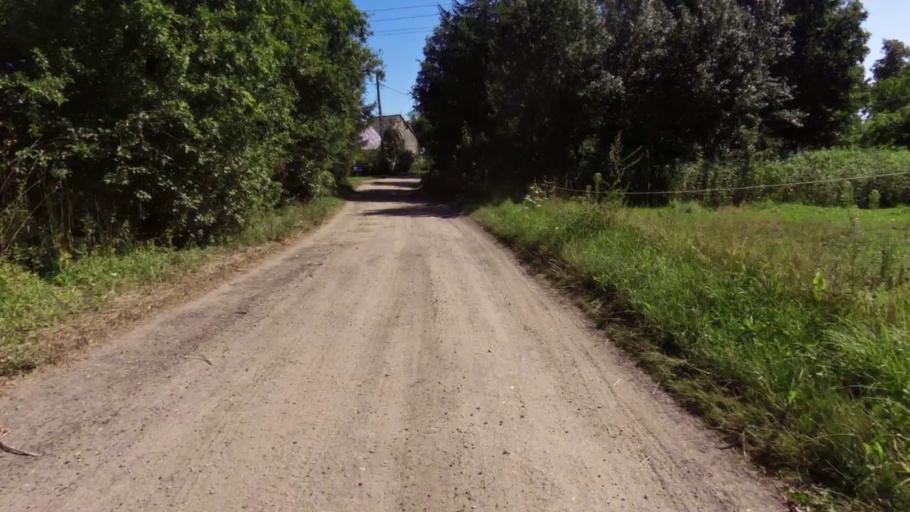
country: PL
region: West Pomeranian Voivodeship
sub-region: Powiat drawski
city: Wierzchowo
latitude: 53.5258
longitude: 16.1533
